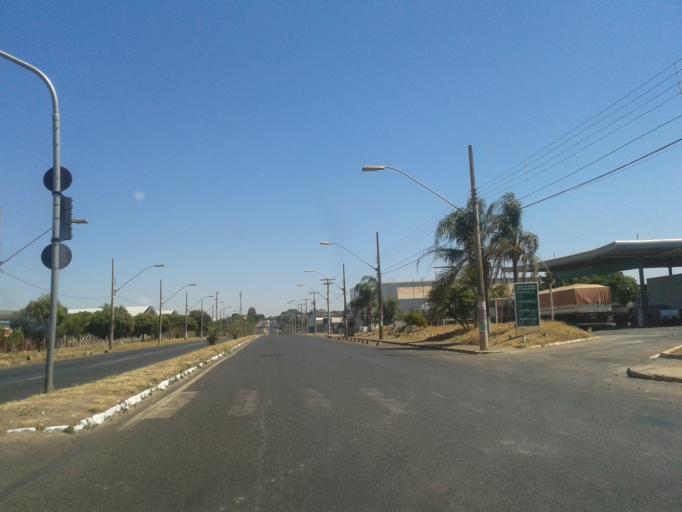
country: BR
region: Minas Gerais
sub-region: Uberlandia
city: Uberlandia
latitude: -18.8749
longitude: -48.2802
